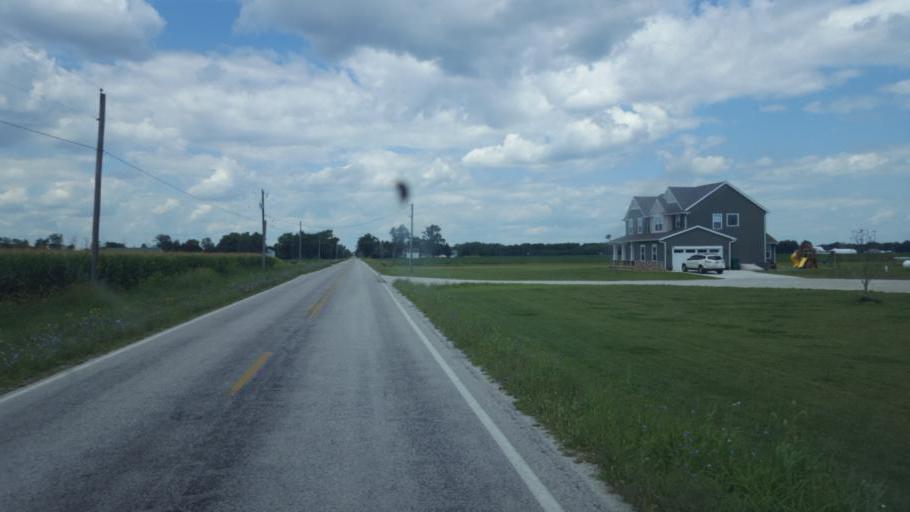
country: US
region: Ohio
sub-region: Ottawa County
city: Elmore
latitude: 41.5297
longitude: -83.2801
